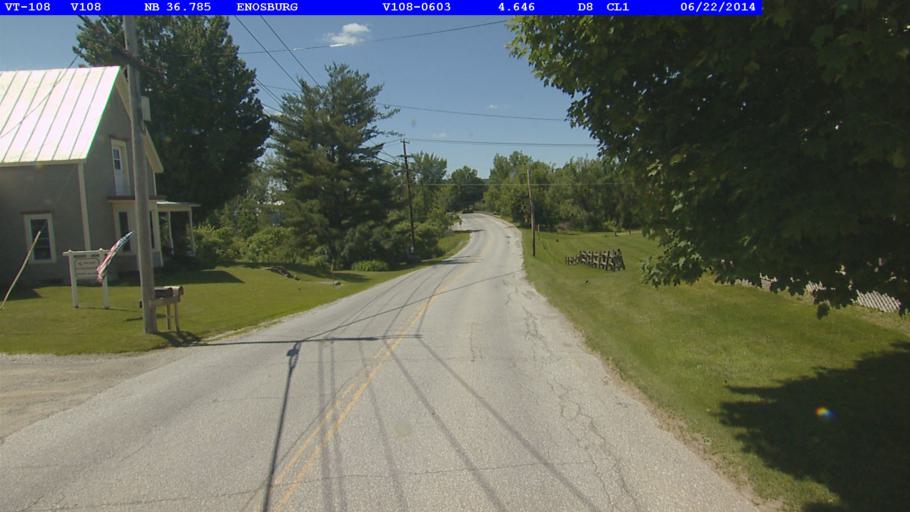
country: US
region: Vermont
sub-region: Franklin County
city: Enosburg Falls
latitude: 44.9014
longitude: -72.8049
